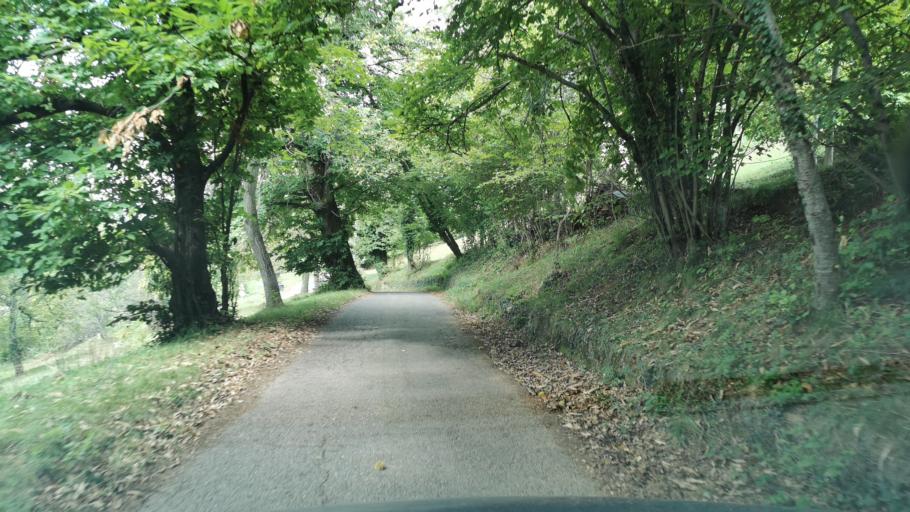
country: IT
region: Piedmont
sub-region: Provincia di Torino
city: Lanzo Torinese
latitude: 45.3006
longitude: 7.4981
